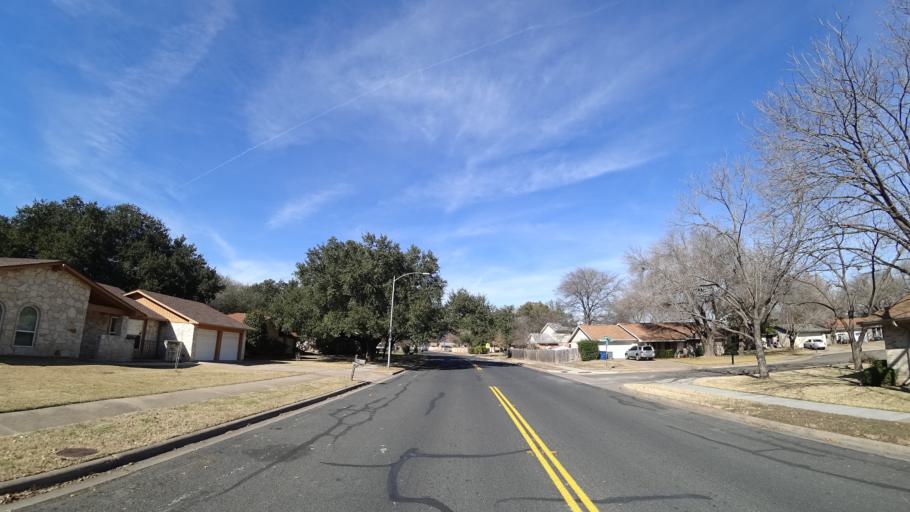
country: US
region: Texas
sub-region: Travis County
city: Wells Branch
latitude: 30.3741
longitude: -97.7042
